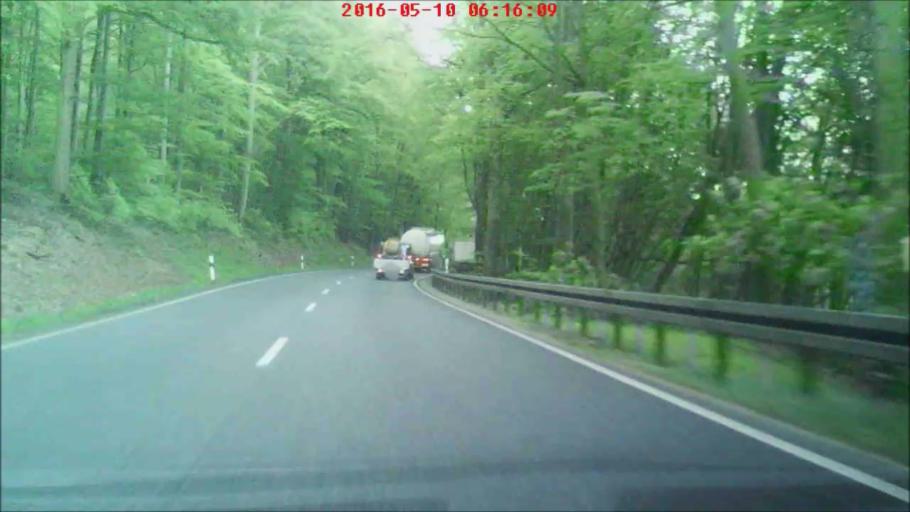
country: DE
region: Hesse
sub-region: Regierungsbezirk Kassel
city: Burghaun
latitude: 50.7459
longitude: 9.6870
